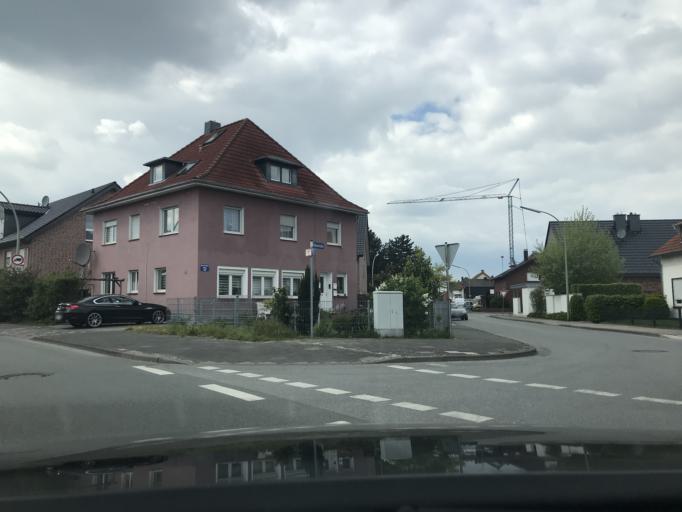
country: DE
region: North Rhine-Westphalia
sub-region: Regierungsbezirk Detmold
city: Rheda-Wiedenbruck
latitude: 51.8581
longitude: 8.2779
